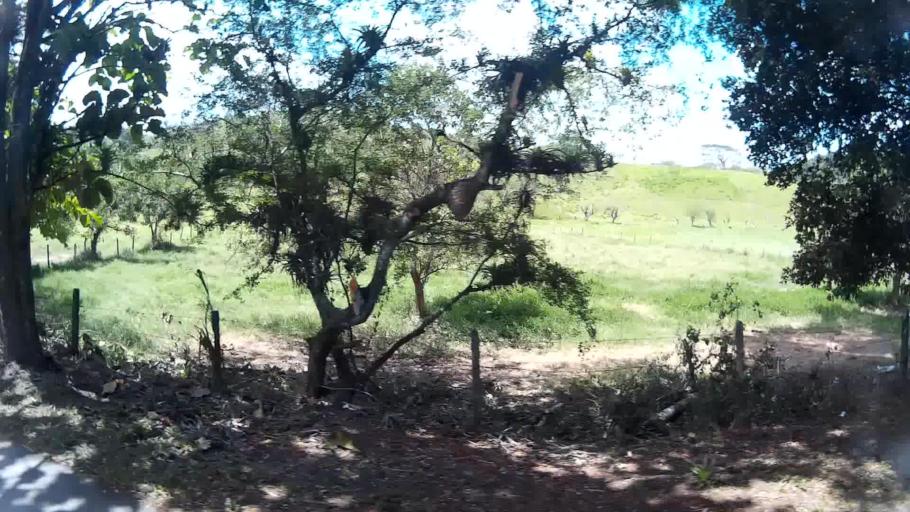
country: CO
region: Risaralda
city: La Virginia
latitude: 4.8982
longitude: -75.8691
